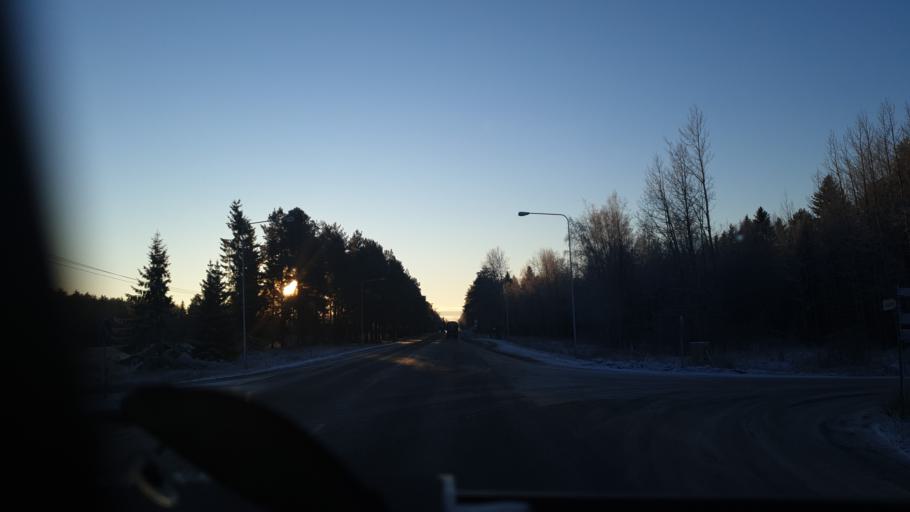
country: FI
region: Northern Ostrobothnia
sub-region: Ylivieska
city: Kalajoki
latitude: 64.2781
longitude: 23.9486
